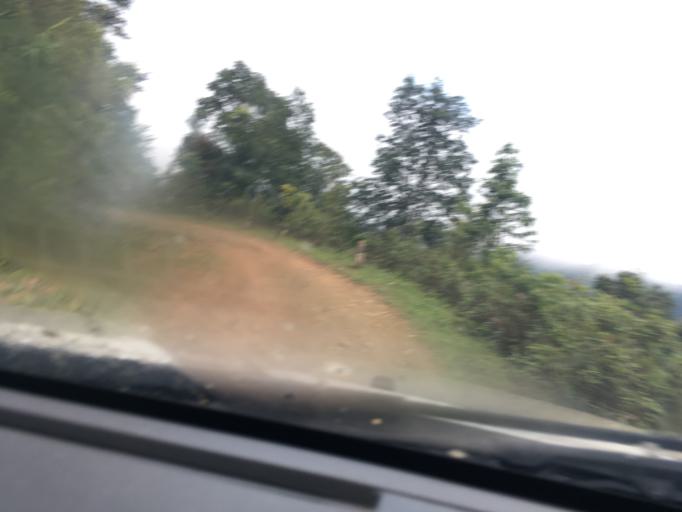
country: LA
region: Phongsali
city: Phongsali
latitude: 21.4272
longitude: 102.2632
